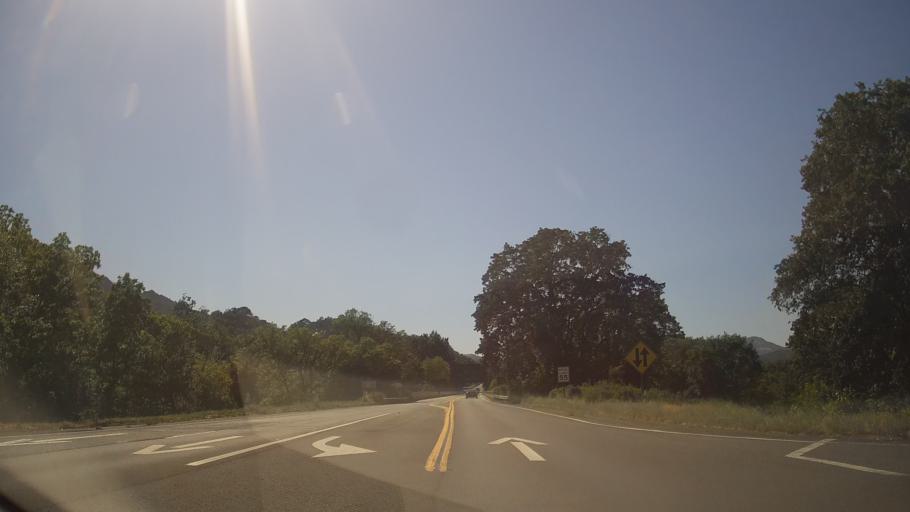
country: US
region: California
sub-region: Sonoma County
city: Cloverdale
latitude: 38.9529
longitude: -123.0985
